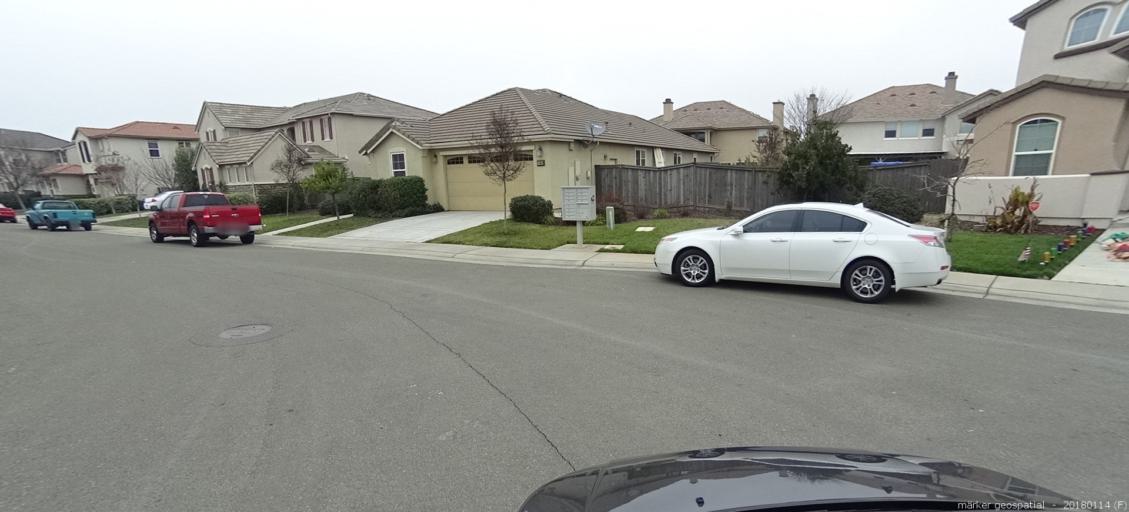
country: US
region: California
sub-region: Sacramento County
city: Rancho Cordova
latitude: 38.5407
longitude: -121.2361
